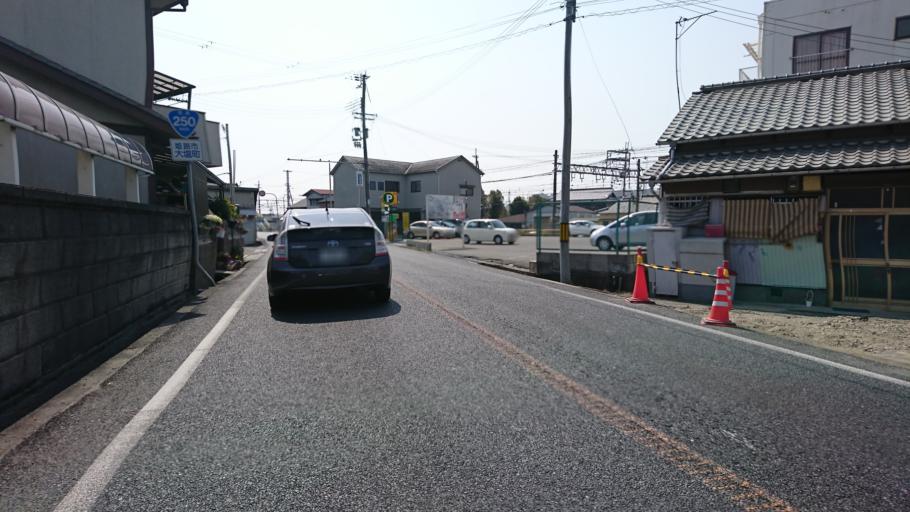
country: JP
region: Hyogo
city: Shirahamacho-usazakiminami
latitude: 34.7794
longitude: 134.7585
